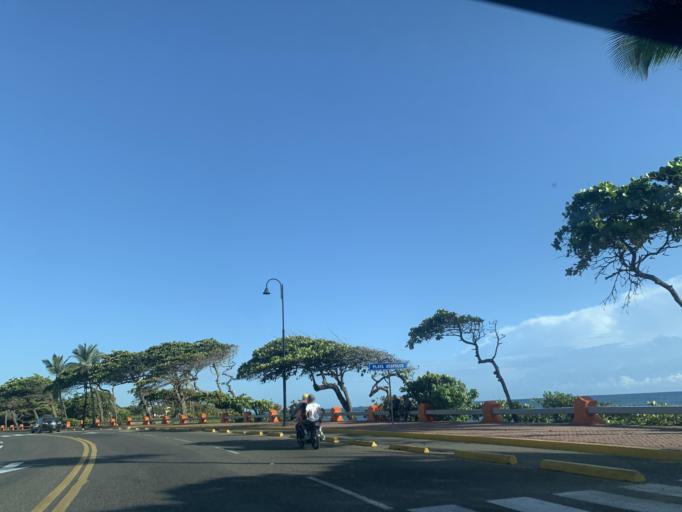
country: DO
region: Puerto Plata
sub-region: Puerto Plata
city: Puerto Plata
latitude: 19.7946
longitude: -70.6805
